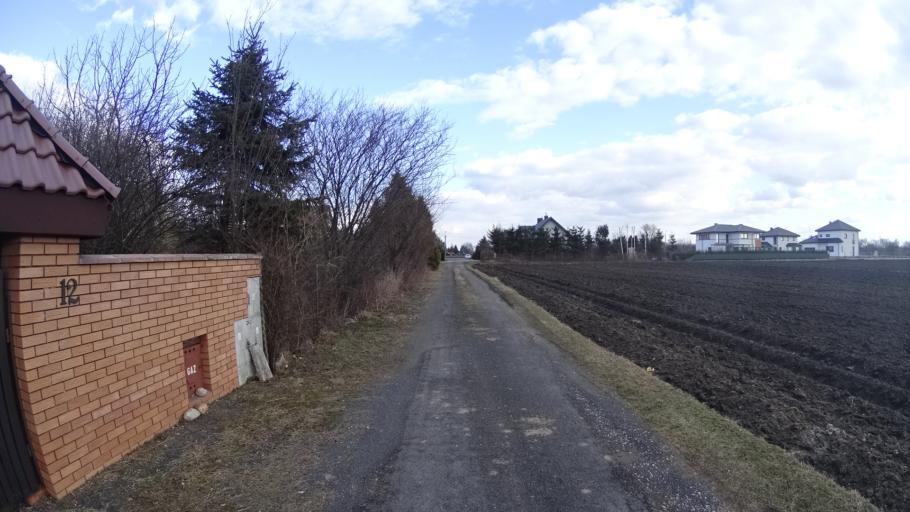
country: PL
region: Masovian Voivodeship
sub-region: Powiat warszawski zachodni
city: Ozarow Mazowiecki
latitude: 52.2457
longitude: 20.7843
